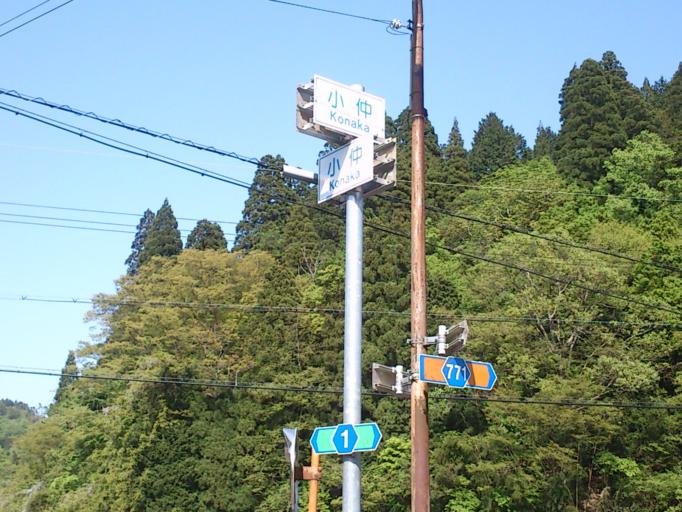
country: JP
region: Kyoto
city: Maizuru
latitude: 35.3876
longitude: 135.4610
